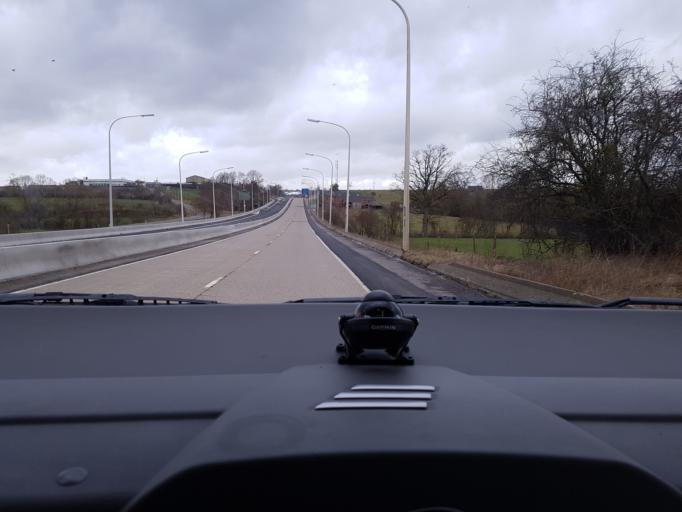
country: BE
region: Wallonia
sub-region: Province de Namur
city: Rochefort
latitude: 50.2711
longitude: 5.2418
